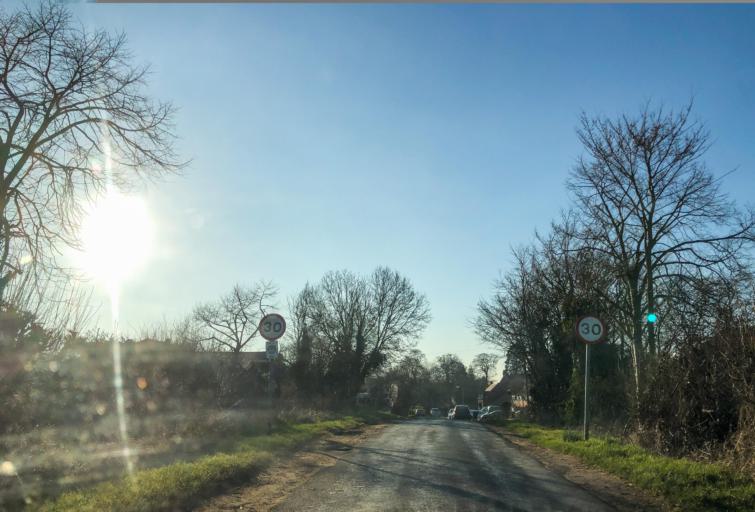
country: GB
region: England
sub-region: Warwickshire
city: Wellesbourne Mountford
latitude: 52.2014
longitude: -1.5403
